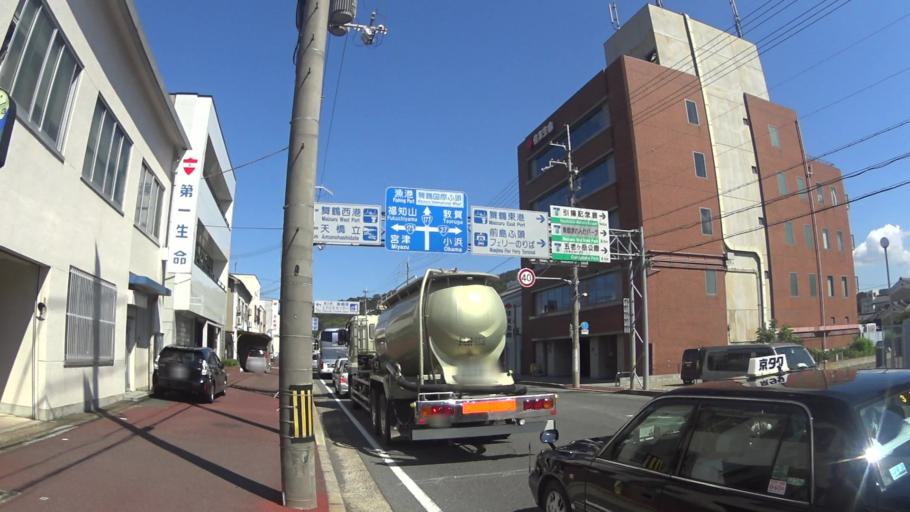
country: JP
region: Kyoto
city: Maizuru
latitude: 35.4496
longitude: 135.3288
